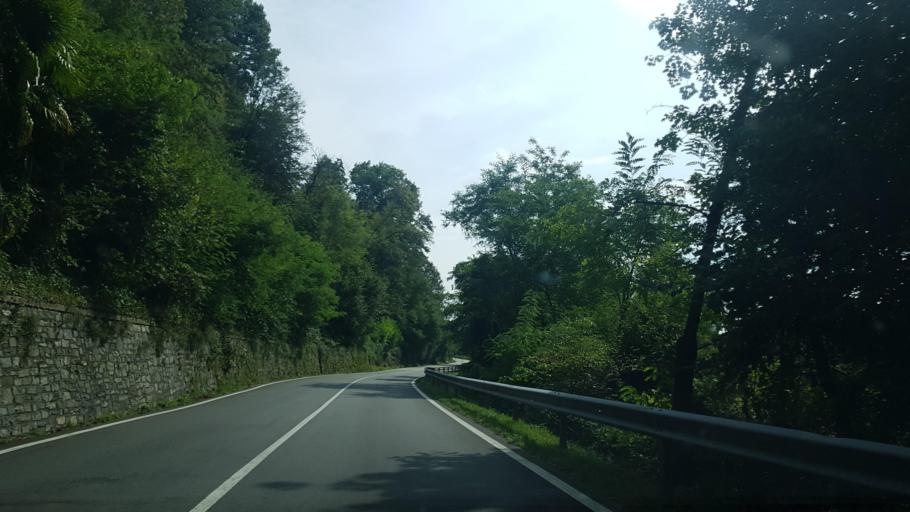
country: IT
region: Piedmont
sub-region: Provincia Verbano-Cusio-Ossola
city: Vignone
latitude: 45.9632
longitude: 8.5670
